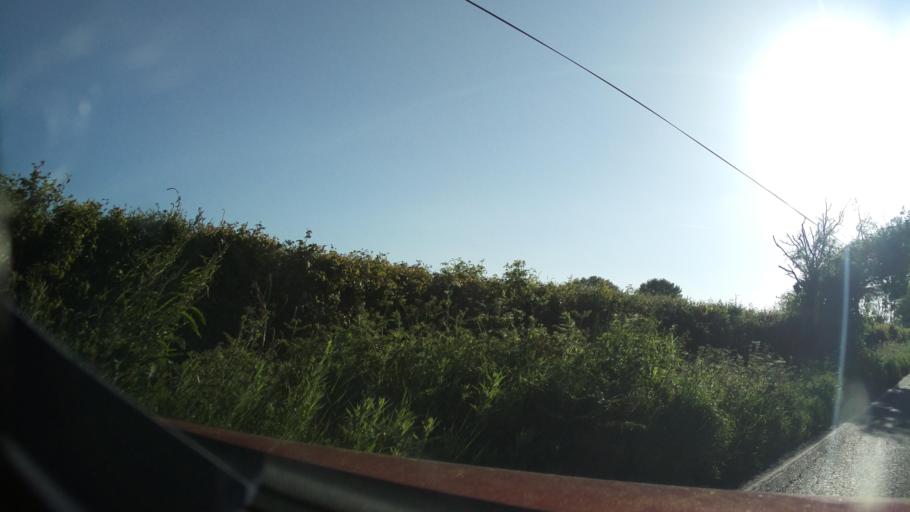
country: GB
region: England
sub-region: Devon
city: Colyton
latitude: 50.7134
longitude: -3.1415
